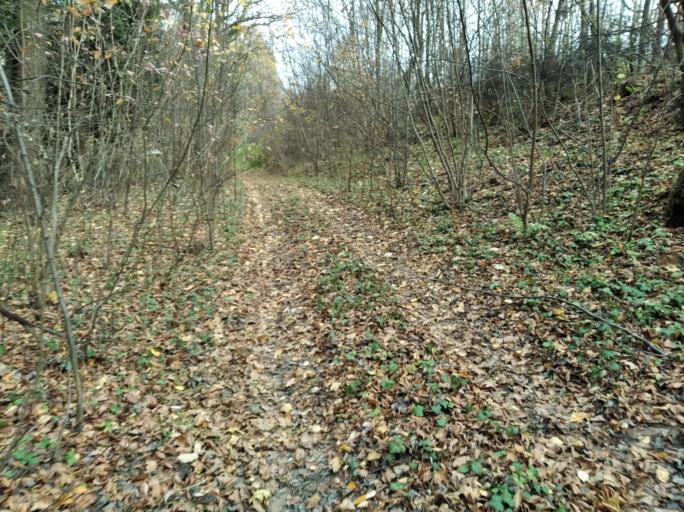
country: PL
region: Subcarpathian Voivodeship
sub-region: Powiat strzyzowski
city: Jawornik
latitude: 49.8490
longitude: 21.8444
